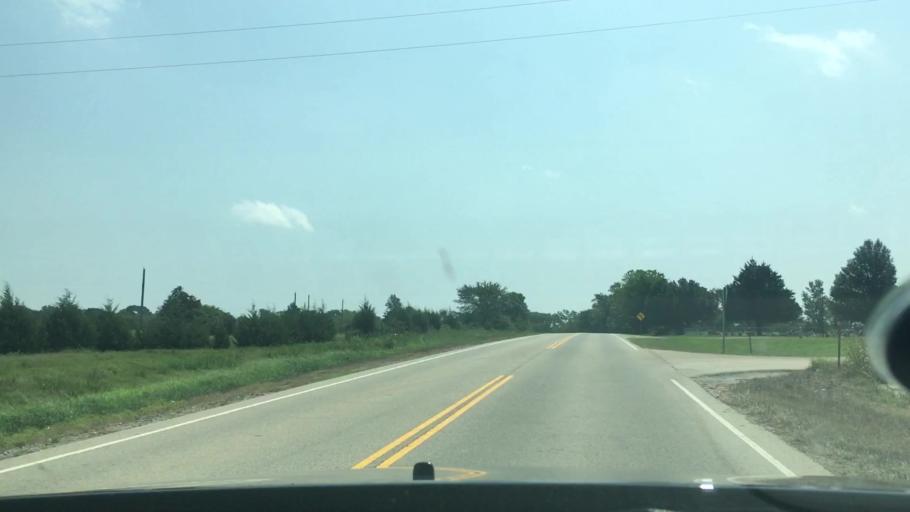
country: US
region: Oklahoma
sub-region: Atoka County
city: Atoka
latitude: 34.2827
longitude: -95.9538
